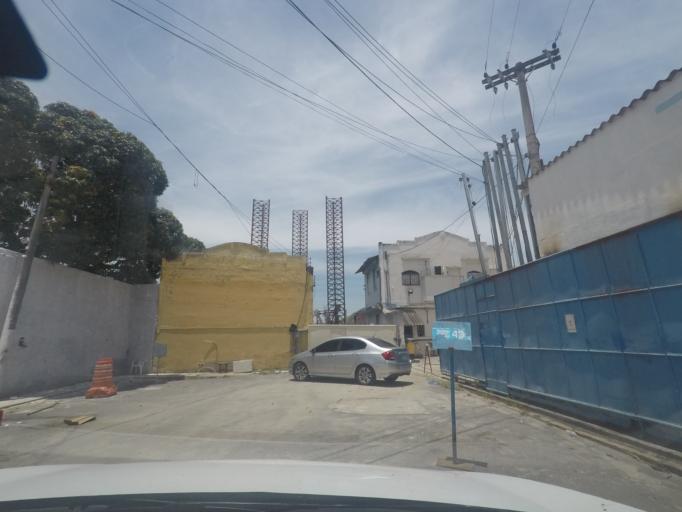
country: BR
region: Rio de Janeiro
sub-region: Niteroi
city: Niteroi
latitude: -22.8825
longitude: -43.1209
